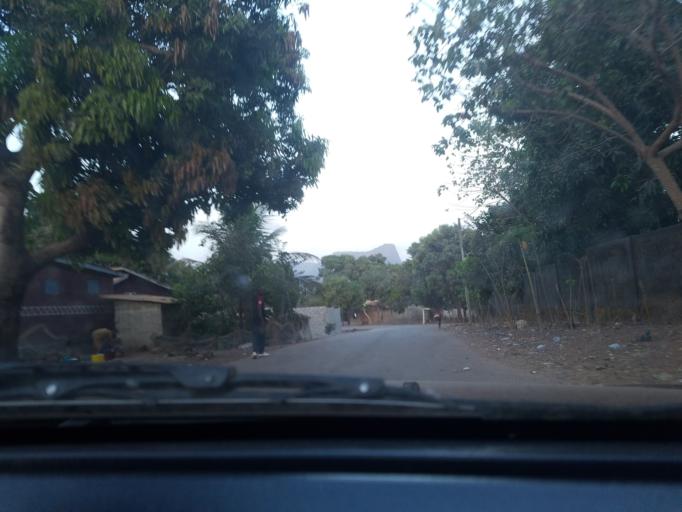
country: GN
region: Kindia
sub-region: Prefecture de Dubreka
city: Dubreka
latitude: 9.7883
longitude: -13.5161
